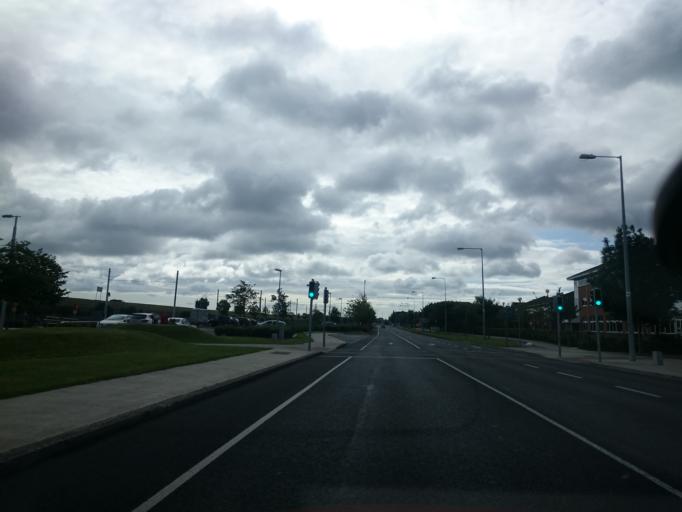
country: IE
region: Leinster
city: Sandyford
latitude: 53.2791
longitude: -6.2105
